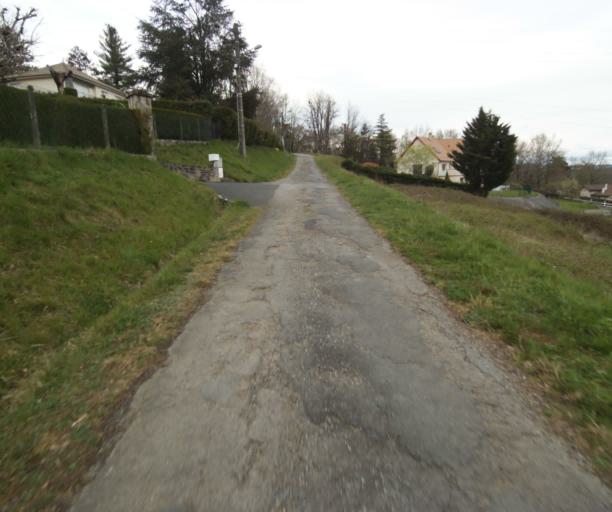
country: FR
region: Limousin
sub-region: Departement de la Correze
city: Tulle
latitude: 45.2528
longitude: 1.7702
